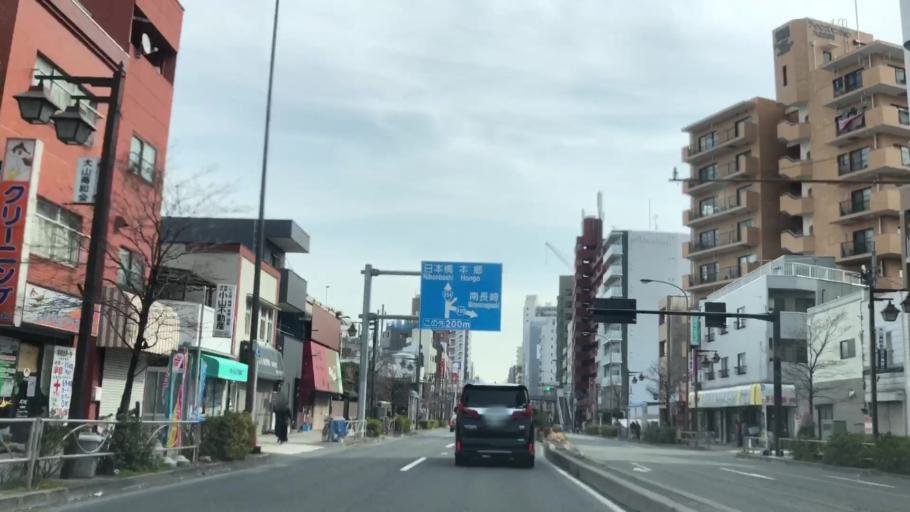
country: JP
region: Saitama
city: Kawaguchi
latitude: 35.7498
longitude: 139.6959
